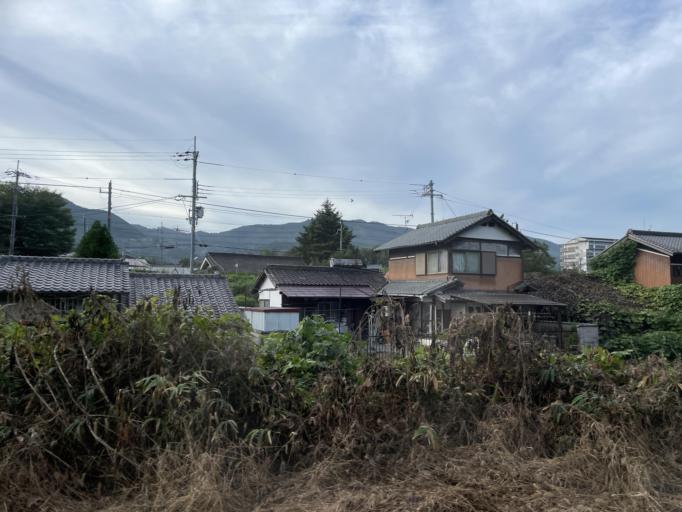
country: JP
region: Wakayama
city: Hashimoto
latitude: 34.3200
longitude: 135.6195
